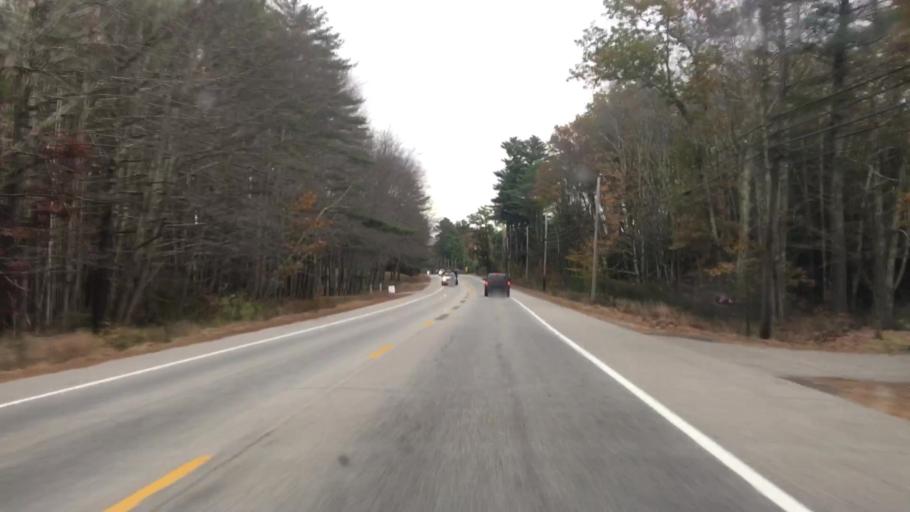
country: US
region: Maine
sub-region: York County
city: Alfred
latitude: 43.4758
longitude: -70.6992
